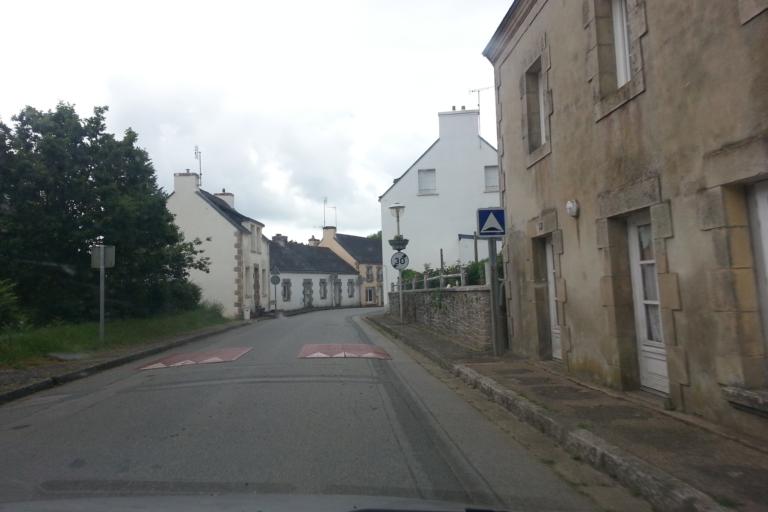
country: FR
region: Brittany
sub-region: Departement du Morbihan
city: Lanvenegen
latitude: 47.9997
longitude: -3.5393
